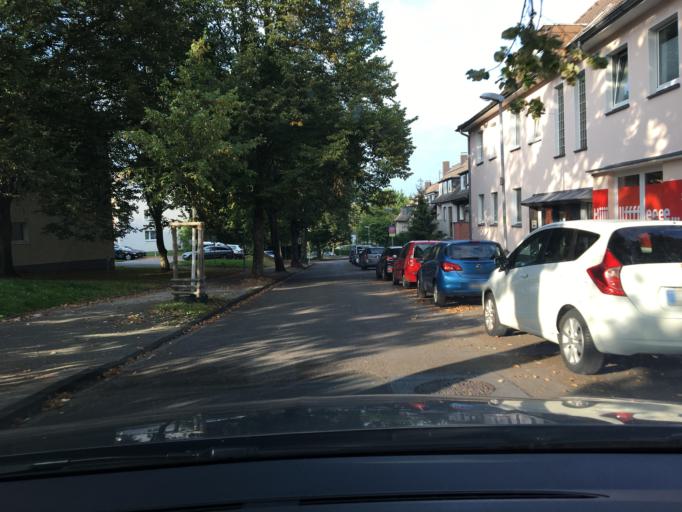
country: DE
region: North Rhine-Westphalia
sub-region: Regierungsbezirk Dusseldorf
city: Essen
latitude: 51.4461
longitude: 7.0586
